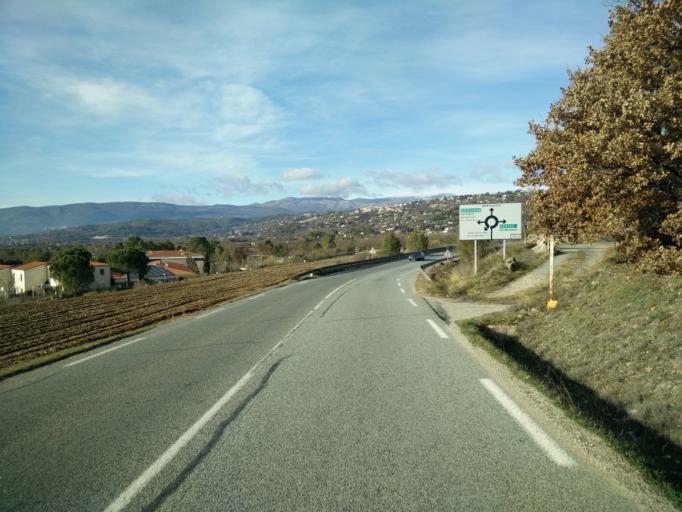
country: FR
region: Provence-Alpes-Cote d'Azur
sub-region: Departement du Var
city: Montauroux
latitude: 43.5973
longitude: 6.7868
